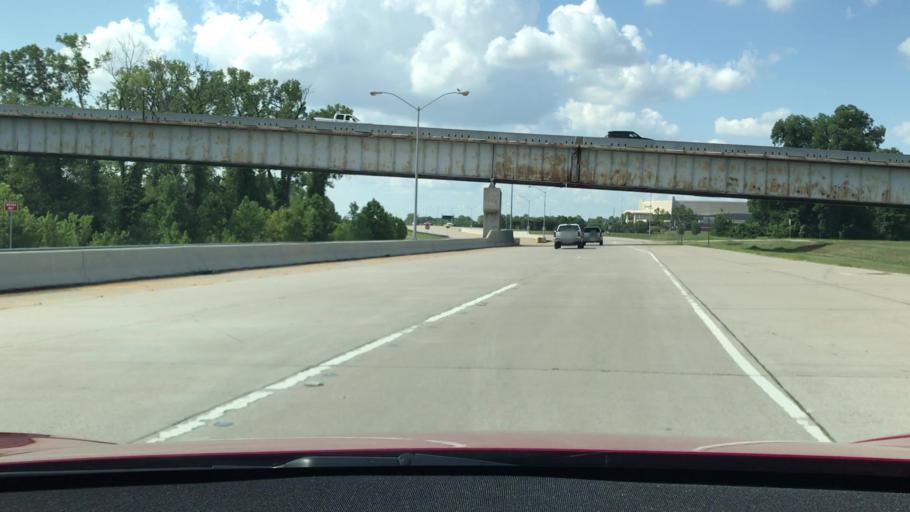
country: US
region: Louisiana
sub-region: Bossier Parish
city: Bossier City
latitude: 32.4581
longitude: -93.6755
